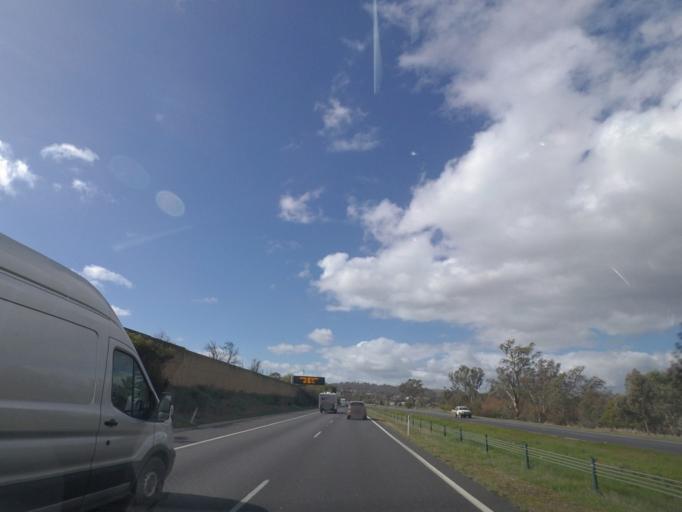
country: AU
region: New South Wales
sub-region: Albury Municipality
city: South Albury
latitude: -36.0979
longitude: 146.9152
